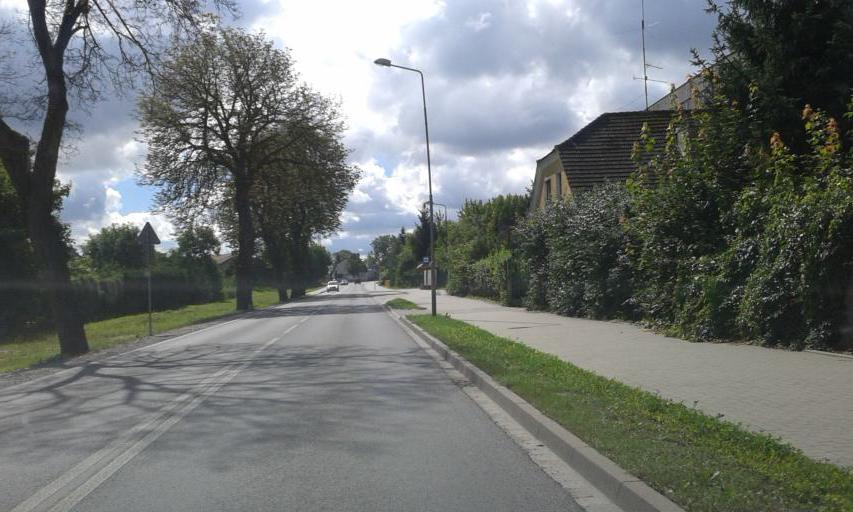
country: PL
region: West Pomeranian Voivodeship
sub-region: Powiat walecki
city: Walcz
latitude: 53.2822
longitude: 16.4626
